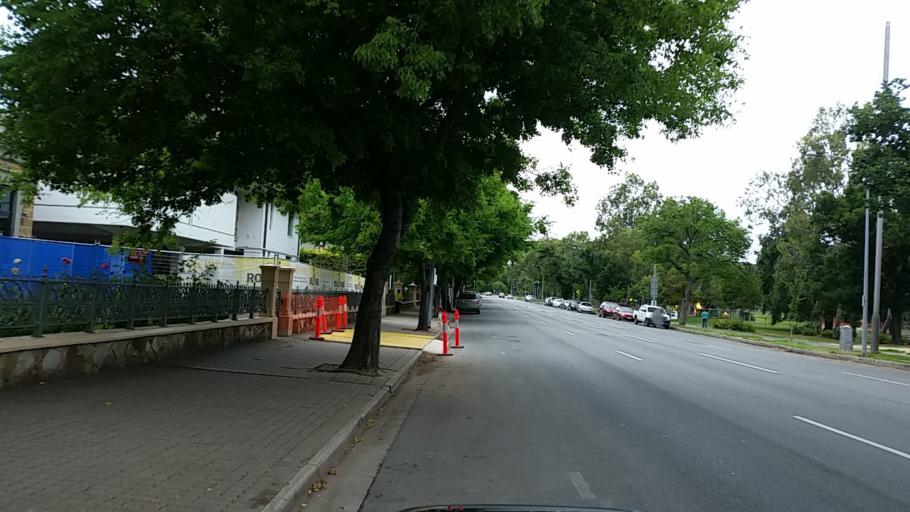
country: AU
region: South Australia
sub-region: Adelaide
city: Adelaide
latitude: -34.9354
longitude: 138.6031
